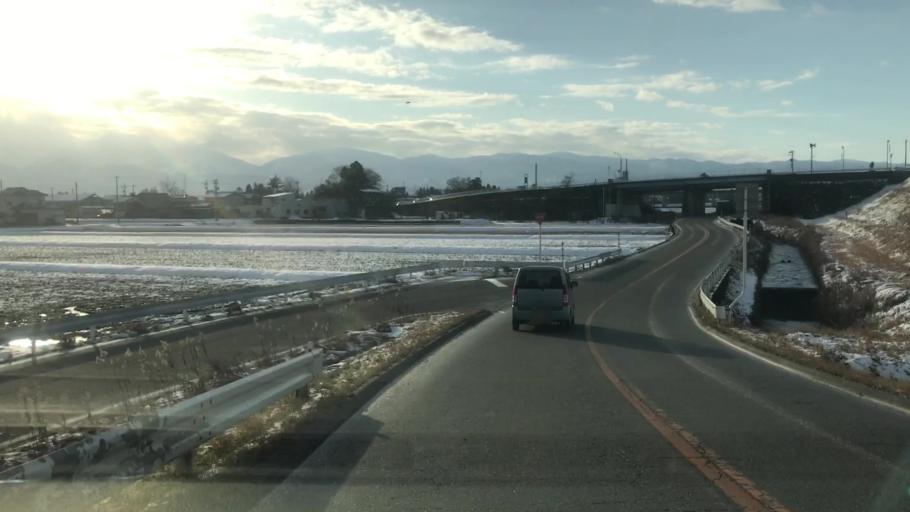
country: JP
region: Toyama
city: Toyama-shi
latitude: 36.6741
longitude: 137.2862
